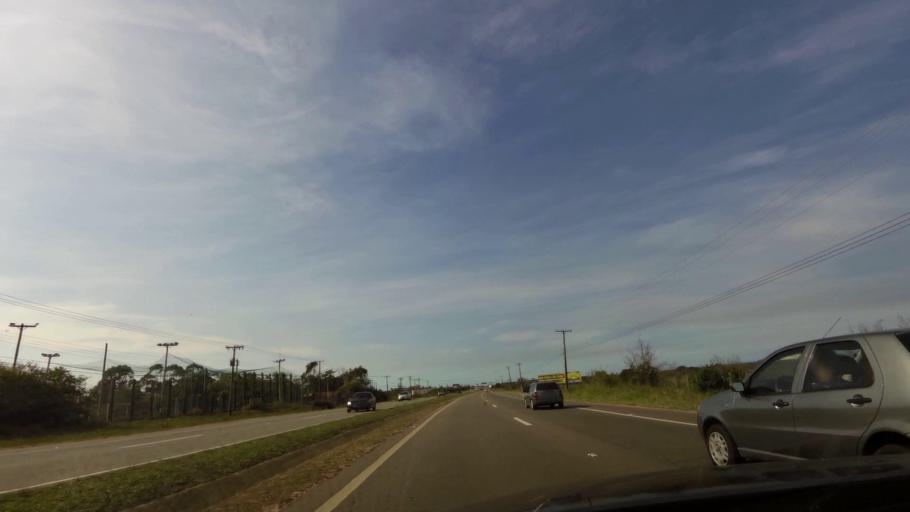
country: BR
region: Espirito Santo
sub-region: Vila Velha
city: Vila Velha
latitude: -20.4585
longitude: -40.3421
